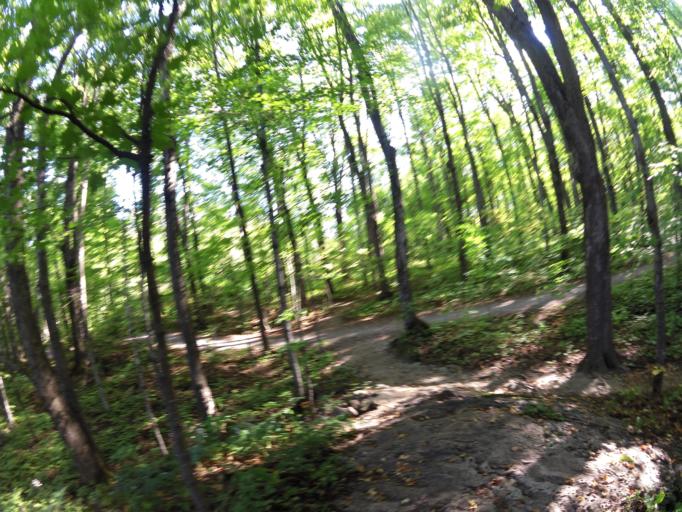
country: CA
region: Ontario
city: Bells Corners
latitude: 45.3389
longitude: -75.9293
